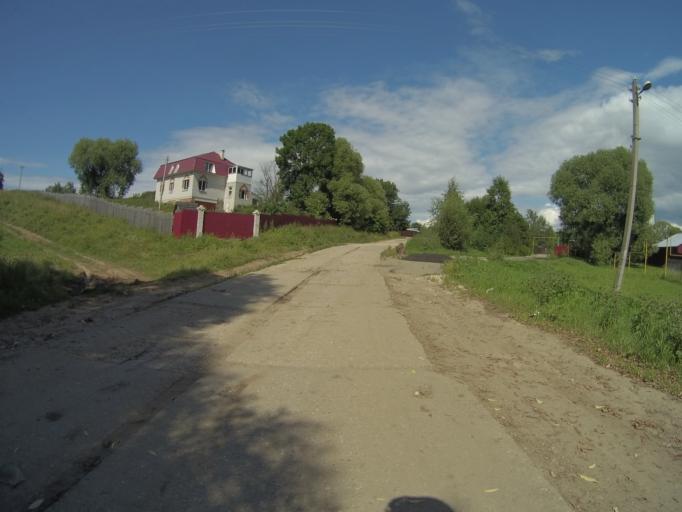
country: RU
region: Vladimir
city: Vladimir
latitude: 56.2658
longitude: 40.3771
